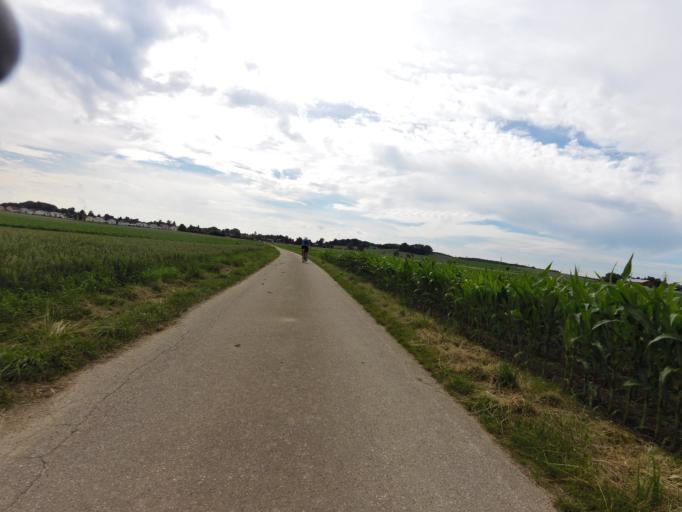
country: DE
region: Bavaria
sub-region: Upper Bavaria
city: Hebertshausen
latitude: 48.3079
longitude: 11.5001
